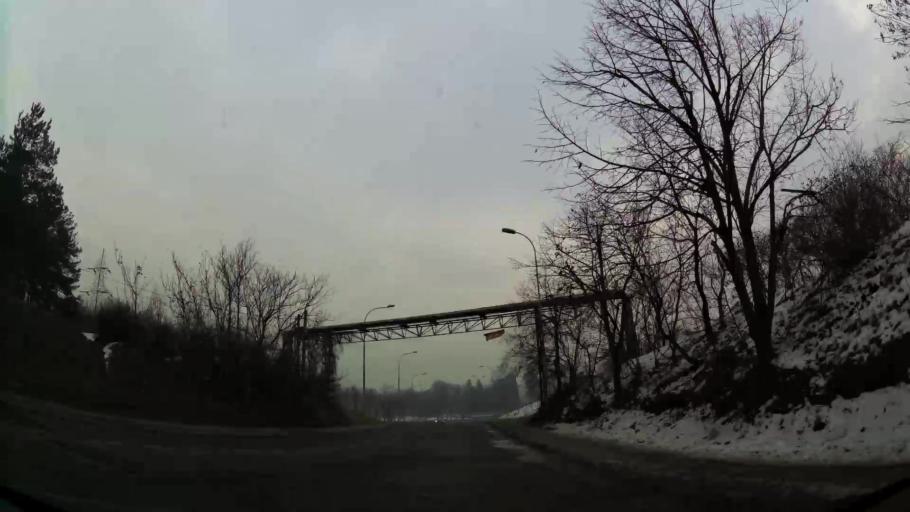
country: MK
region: Cair
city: Cair
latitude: 42.0078
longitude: 21.4623
